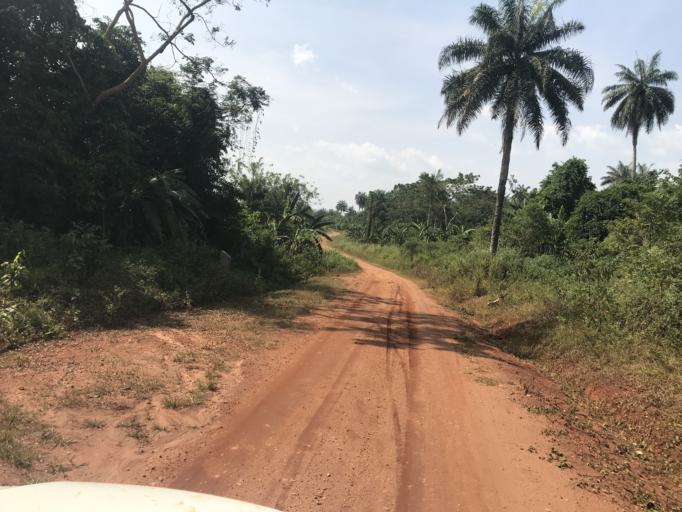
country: NG
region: Osun
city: Osu
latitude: 7.6346
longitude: 4.6651
